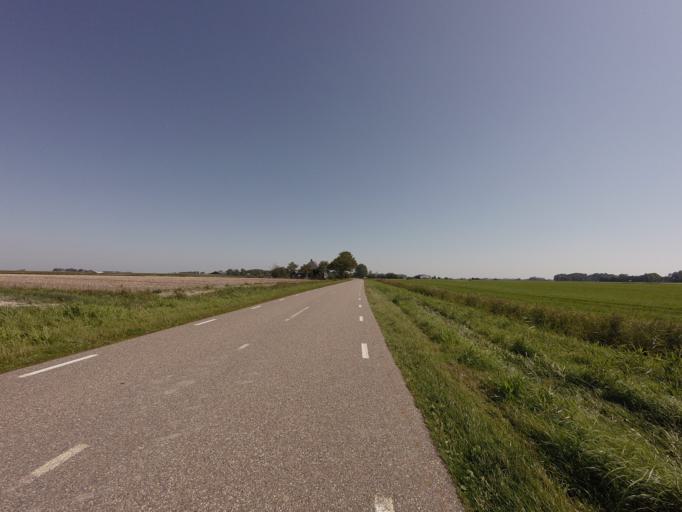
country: NL
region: Friesland
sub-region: Gemeente Dongeradeel
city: Ternaard
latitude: 53.3681
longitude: 5.9853
